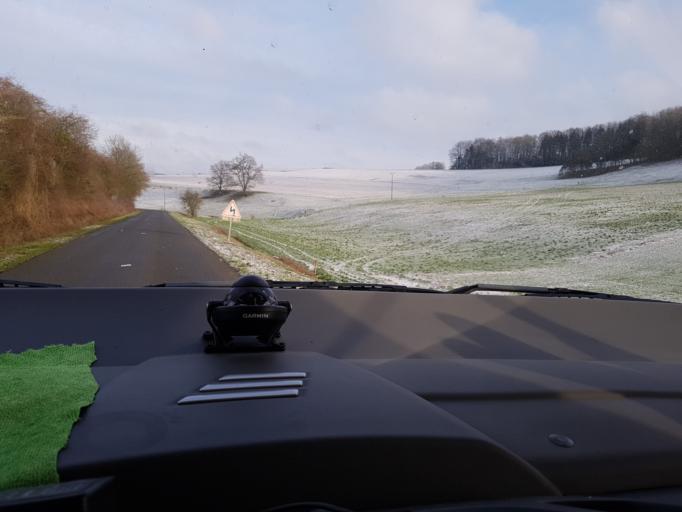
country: FR
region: Champagne-Ardenne
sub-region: Departement des Ardennes
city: Tournes
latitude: 49.7353
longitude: 4.5742
